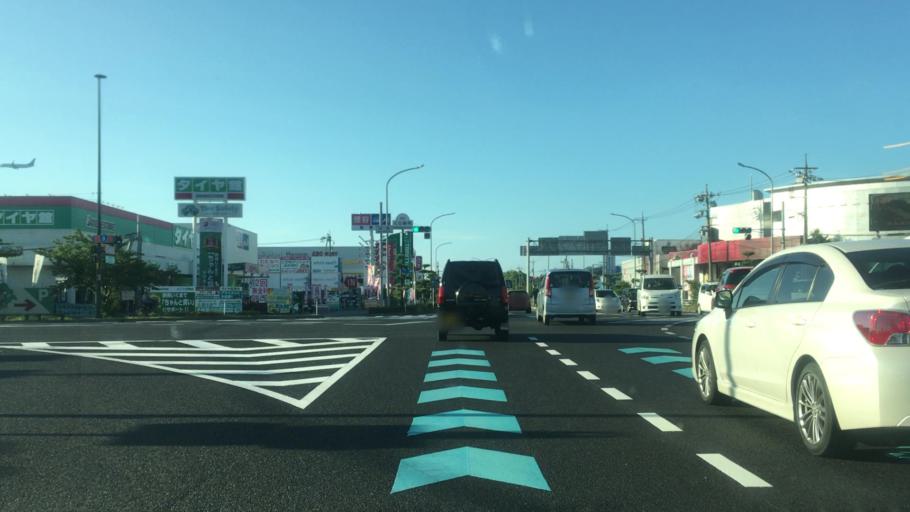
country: JP
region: Tottori
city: Tottori
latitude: 35.5192
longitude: 134.2023
